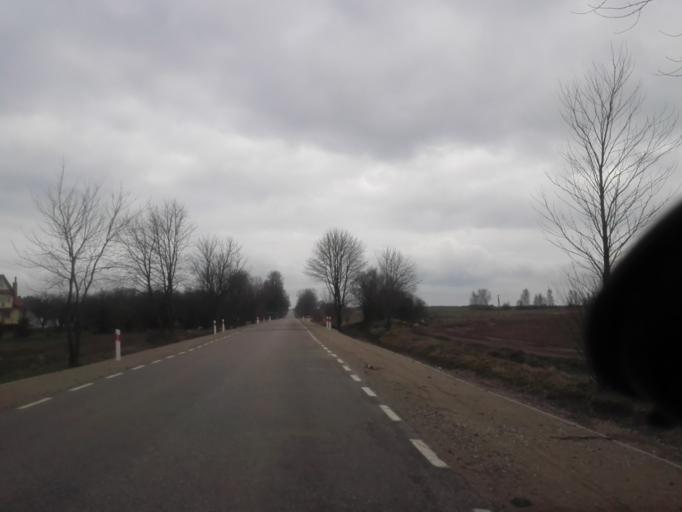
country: PL
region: Podlasie
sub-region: Suwalki
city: Suwalki
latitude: 54.2410
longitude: 22.9158
